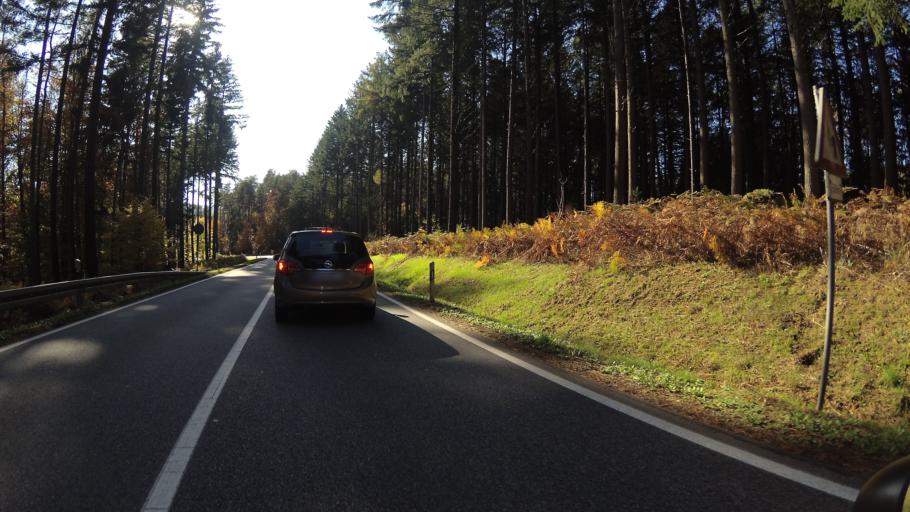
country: DE
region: Saarland
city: Losheim
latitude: 49.4973
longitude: 6.7282
